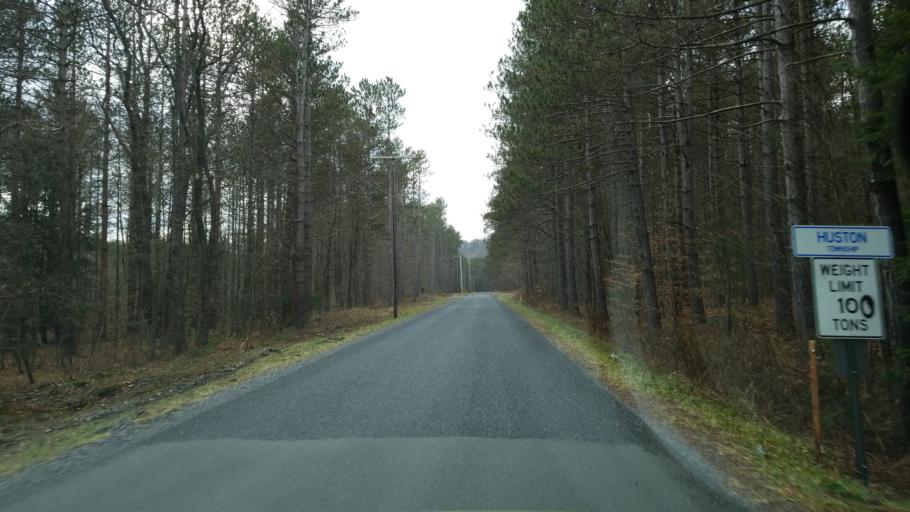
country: US
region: Pennsylvania
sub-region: Clearfield County
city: Treasure Lake
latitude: 41.1480
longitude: -78.5707
